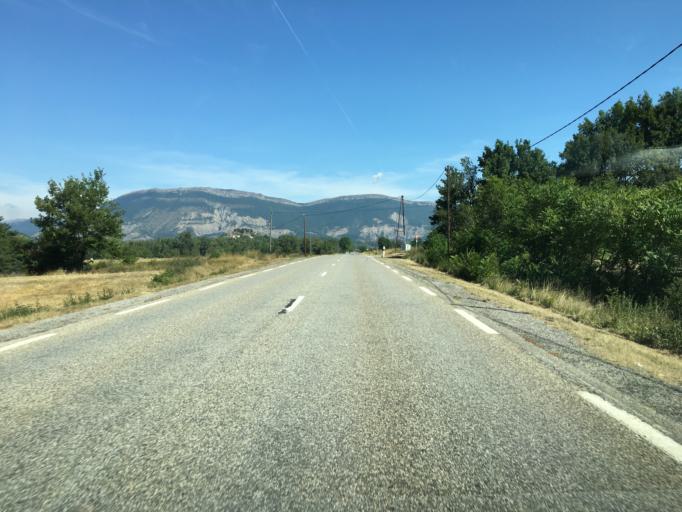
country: FR
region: Provence-Alpes-Cote d'Azur
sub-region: Departement des Hautes-Alpes
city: Serres
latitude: 44.4744
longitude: 5.7263
